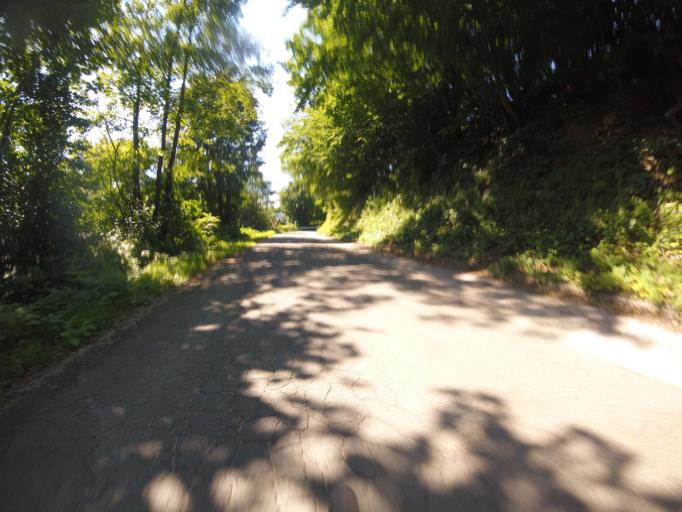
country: SI
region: Brezice
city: Brezice
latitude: 45.8243
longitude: 15.5500
